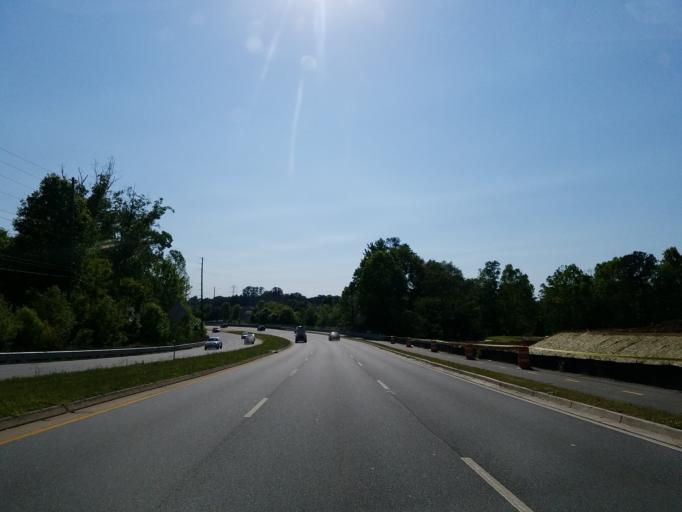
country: US
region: Georgia
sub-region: Cobb County
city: Kennesaw
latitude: 33.9952
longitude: -84.5932
